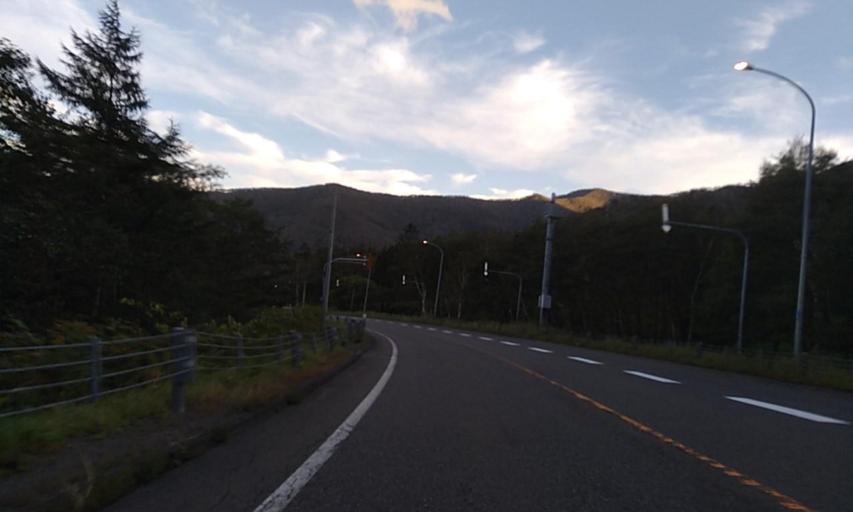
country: JP
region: Hokkaido
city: Otofuke
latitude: 42.9599
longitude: 142.7879
